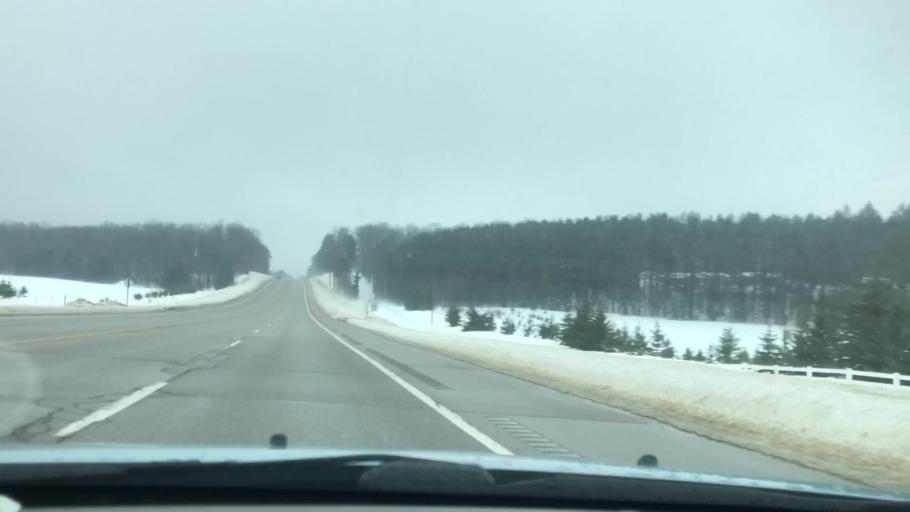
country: US
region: Michigan
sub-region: Otsego County
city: Gaylord
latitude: 45.0531
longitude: -84.7759
